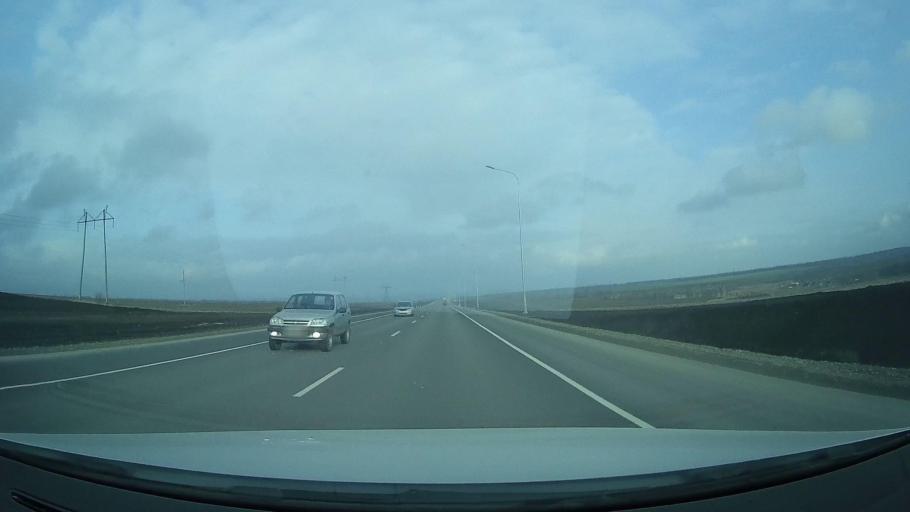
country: RU
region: Rostov
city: Grushevskaya
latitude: 47.3906
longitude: 39.8476
